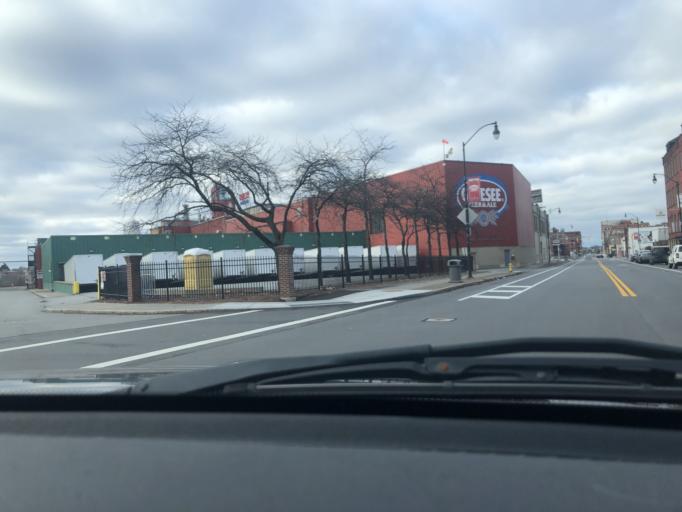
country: US
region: New York
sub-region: Monroe County
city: Rochester
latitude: 43.1638
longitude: -77.6130
